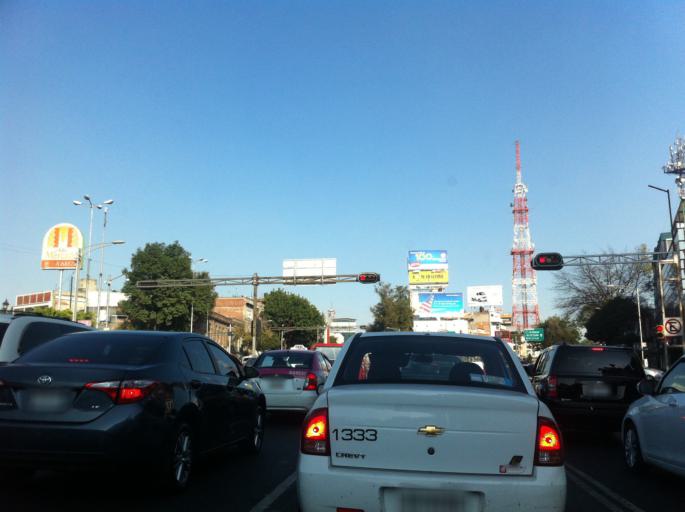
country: MX
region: Mexico City
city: Cuauhtemoc
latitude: 19.4257
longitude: -99.1542
